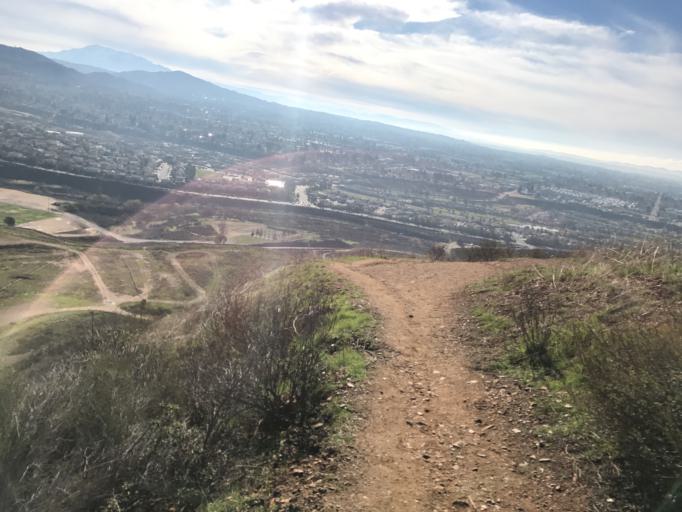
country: US
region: California
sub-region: San Bernardino County
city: Yucaipa
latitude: 34.0518
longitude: -117.0608
